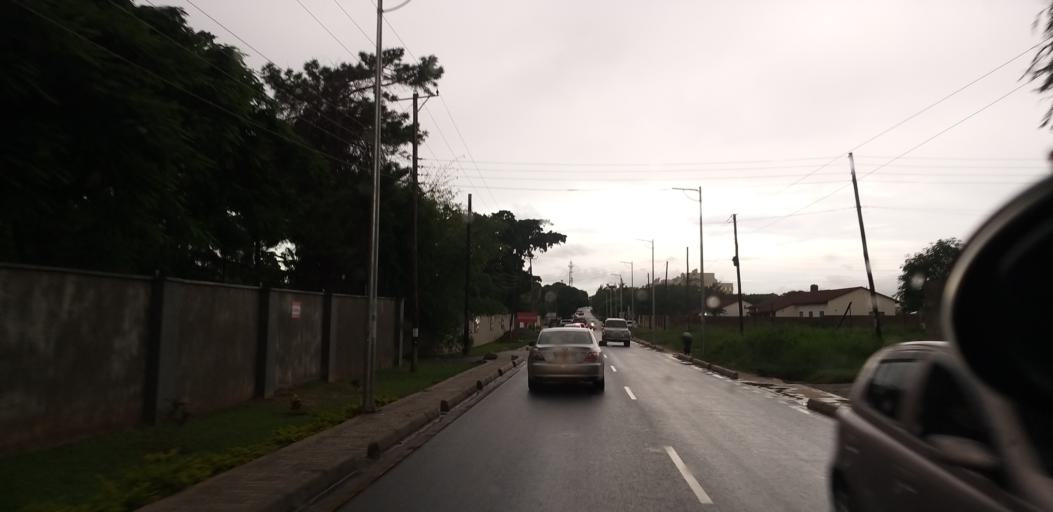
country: ZM
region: Lusaka
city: Lusaka
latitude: -15.4167
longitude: 28.3645
